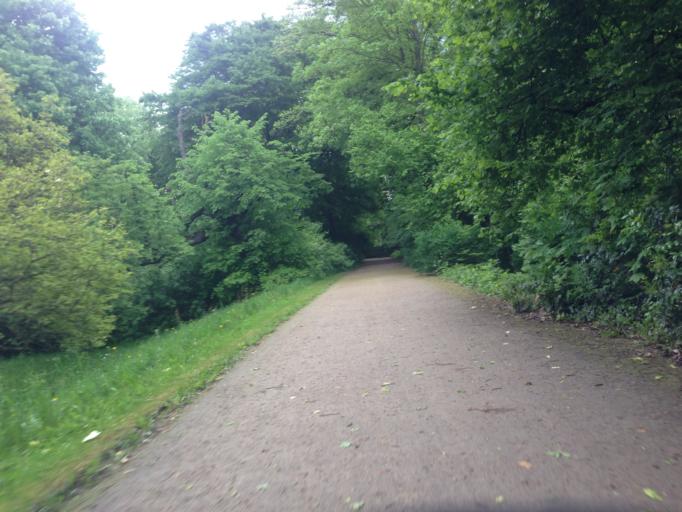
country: DE
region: Saxony
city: Dresden
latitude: 51.0391
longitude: 13.7497
